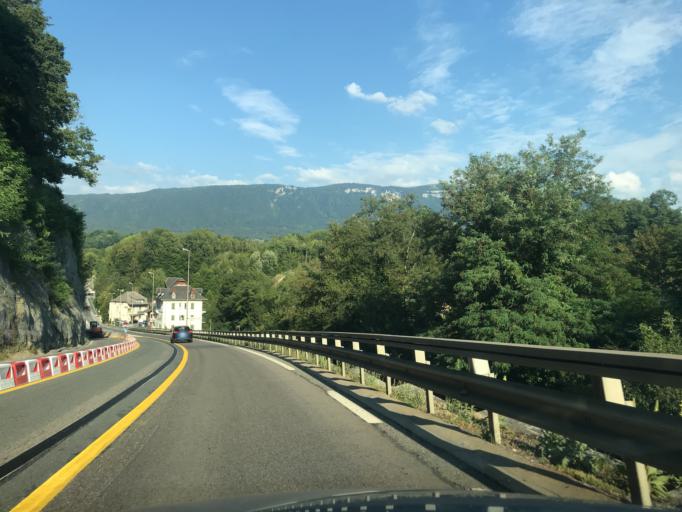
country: FR
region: Rhone-Alpes
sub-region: Departement de la Haute-Savoie
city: Alby-sur-Cheran
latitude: 45.8198
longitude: 6.0203
